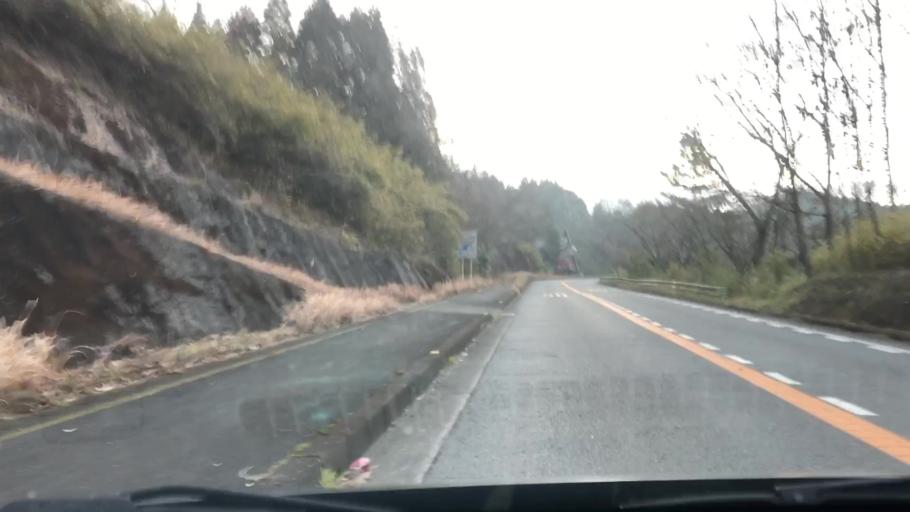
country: JP
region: Oita
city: Takedamachi
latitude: 32.9715
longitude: 131.5040
